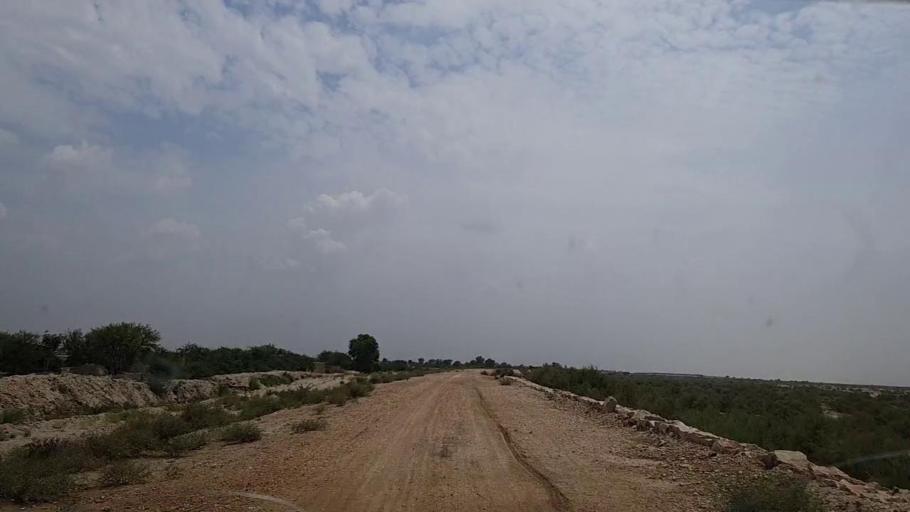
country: PK
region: Sindh
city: Phulji
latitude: 26.8317
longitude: 67.6173
